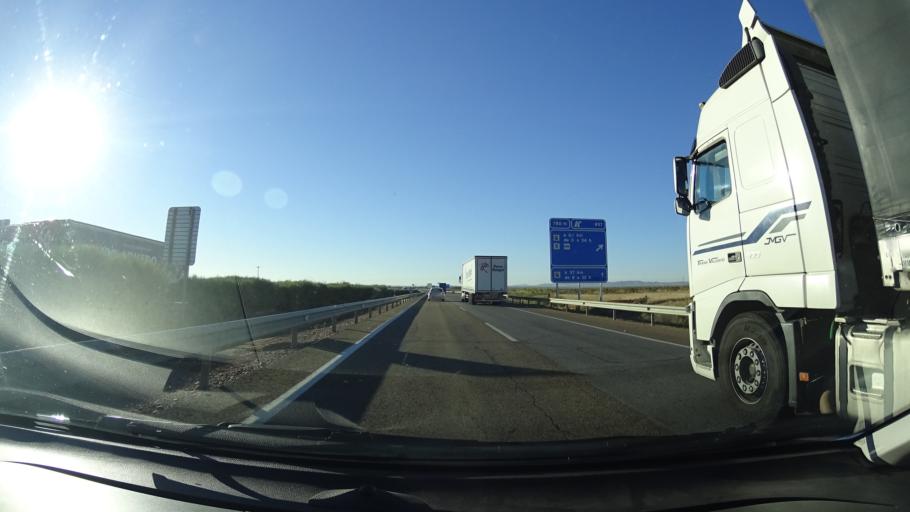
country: ES
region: Extremadura
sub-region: Provincia de Badajoz
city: Almendralejo
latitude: 38.6407
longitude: -6.3745
